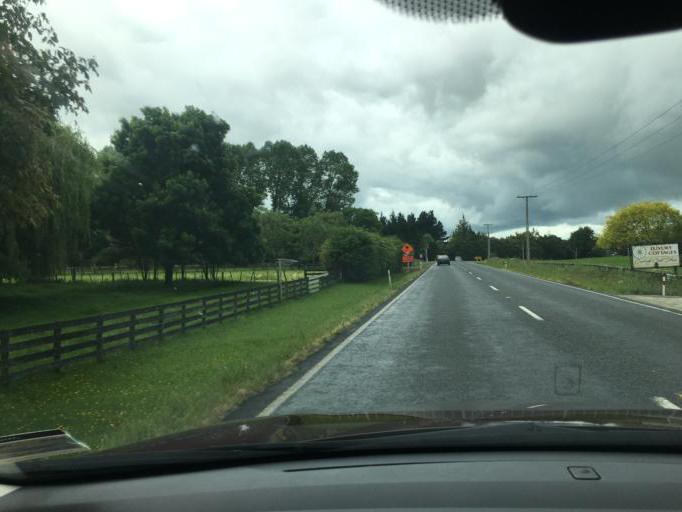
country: NZ
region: Waikato
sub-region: Waipa District
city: Cambridge
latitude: -37.9037
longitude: 175.4516
